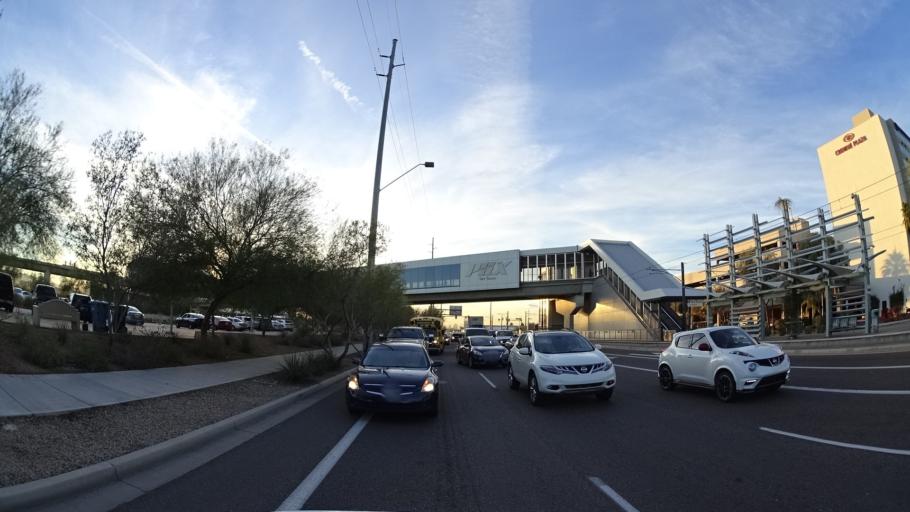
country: US
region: Arizona
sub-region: Maricopa County
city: Tempe Junction
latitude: 33.4480
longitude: -111.9882
